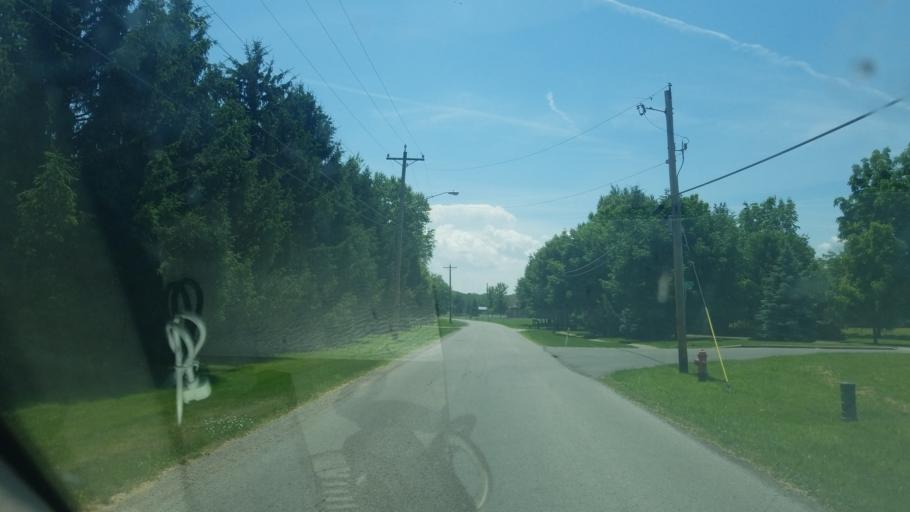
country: US
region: Ohio
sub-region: Hancock County
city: Findlay
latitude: 41.0109
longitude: -83.6361
